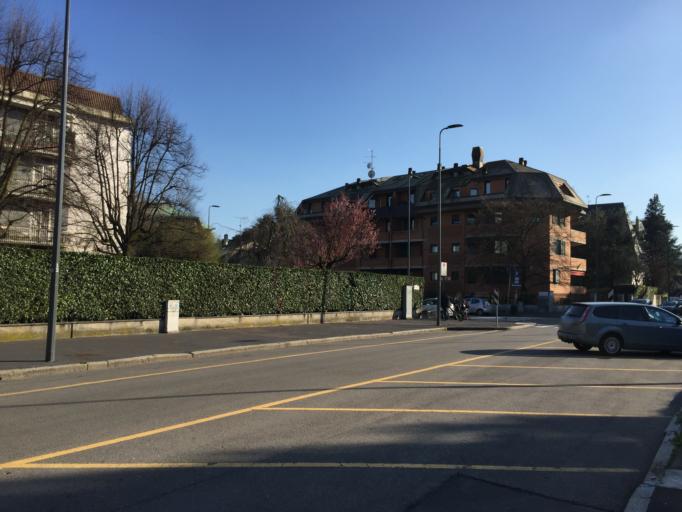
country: IT
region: Lombardy
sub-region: Citta metropolitana di Milano
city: Romano Banco
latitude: 45.4784
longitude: 9.1356
